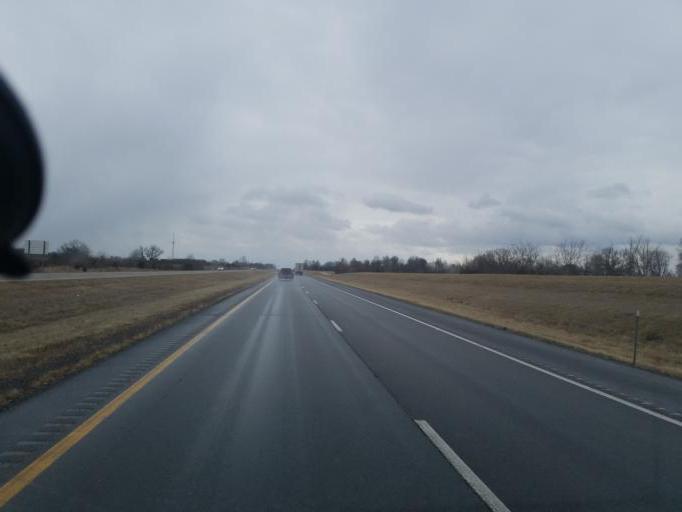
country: US
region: Missouri
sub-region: Randolph County
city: Moberly
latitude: 39.3623
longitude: -92.4033
